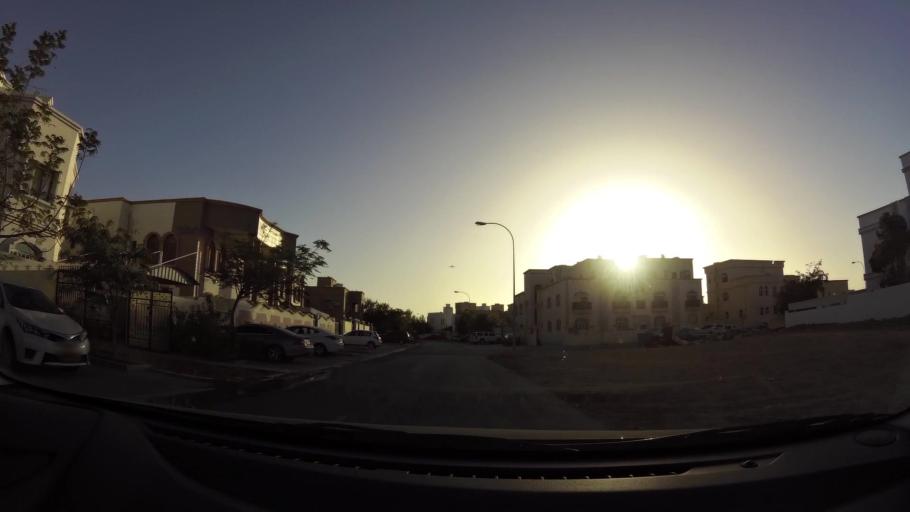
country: OM
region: Muhafazat Masqat
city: As Sib al Jadidah
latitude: 23.6025
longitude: 58.2239
